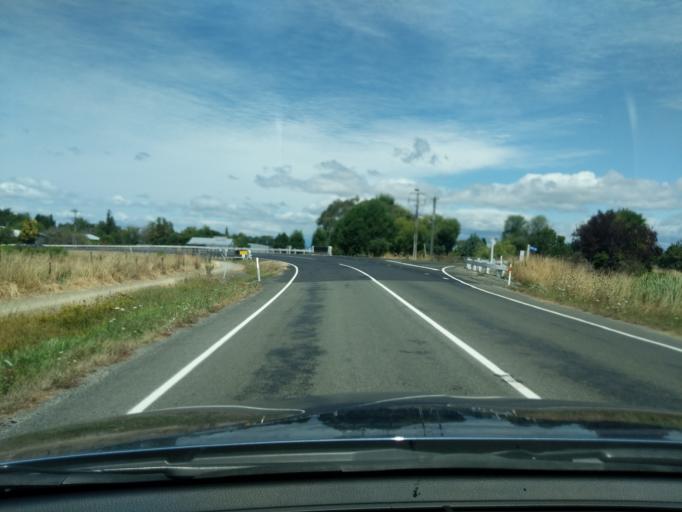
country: NZ
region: Tasman
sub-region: Tasman District
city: Motueka
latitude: -41.0751
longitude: 172.9952
